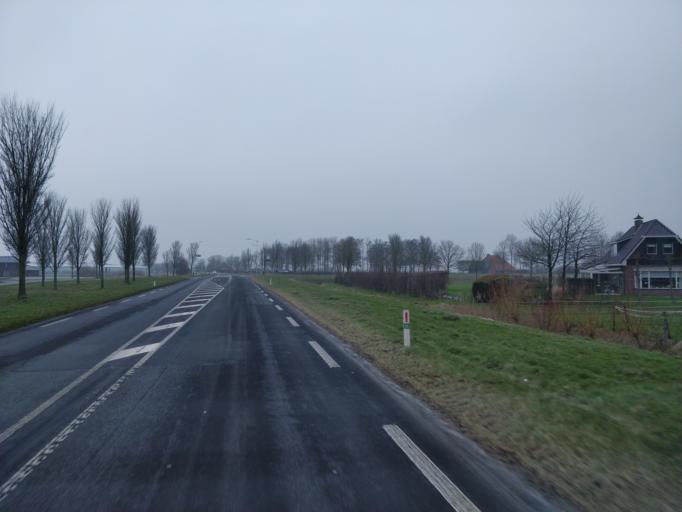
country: NL
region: Friesland
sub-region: Menameradiel
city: Menaam
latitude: 53.2373
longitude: 5.6803
